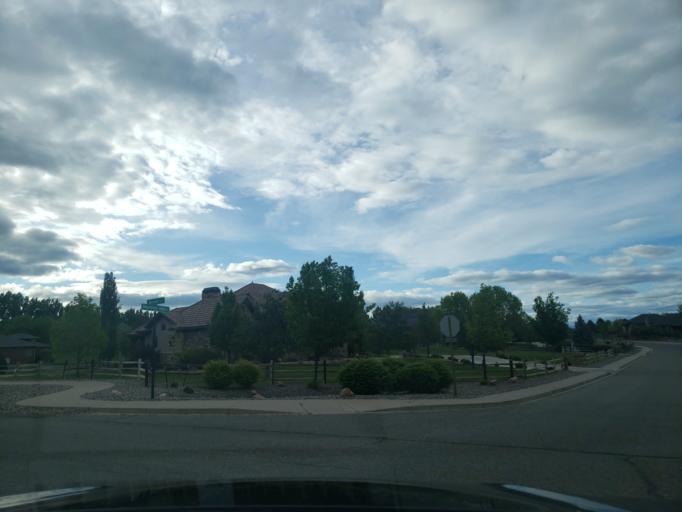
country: US
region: Colorado
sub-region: Mesa County
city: Redlands
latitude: 39.1063
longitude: -108.6746
